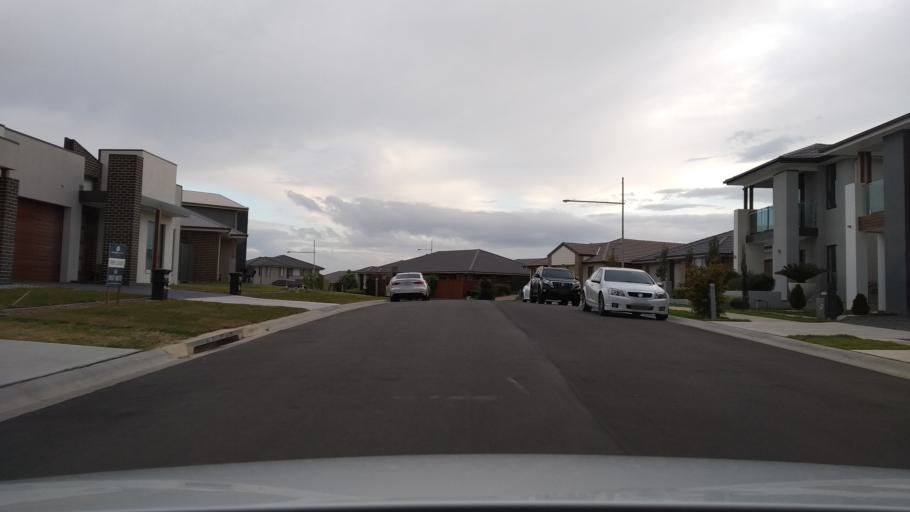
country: AU
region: New South Wales
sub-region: Camden
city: Narellan
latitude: -34.0019
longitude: 150.7294
